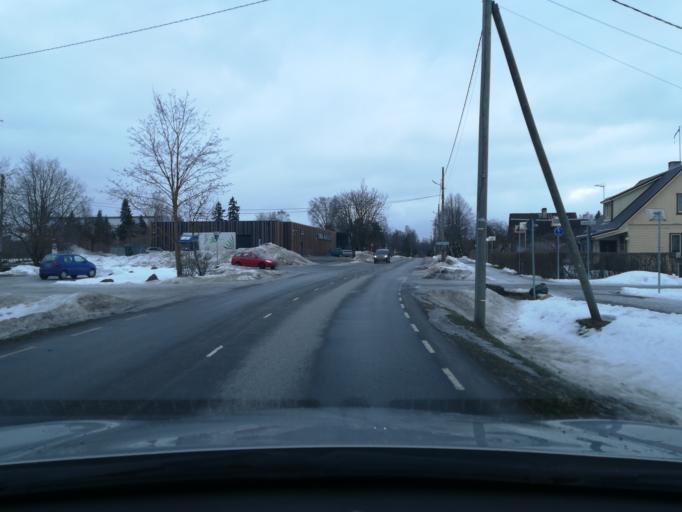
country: EE
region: Harju
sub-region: Nissi vald
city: Turba
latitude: 59.0814
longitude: 24.2360
